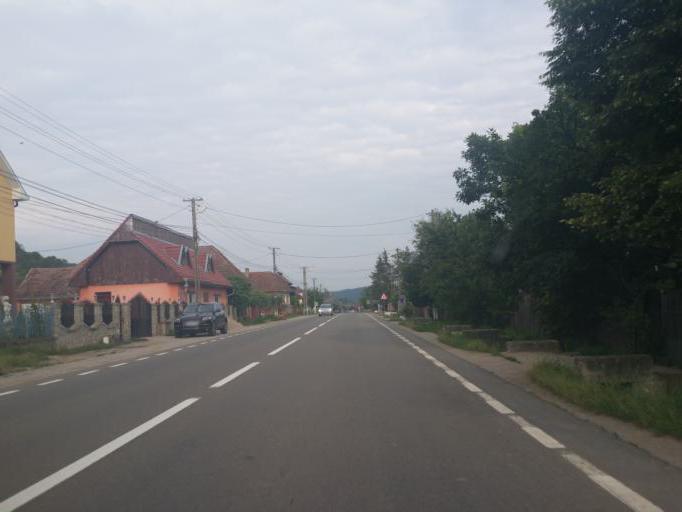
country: RO
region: Salaj
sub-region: Comuna Hida
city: Hida
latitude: 47.0470
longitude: 23.2473
